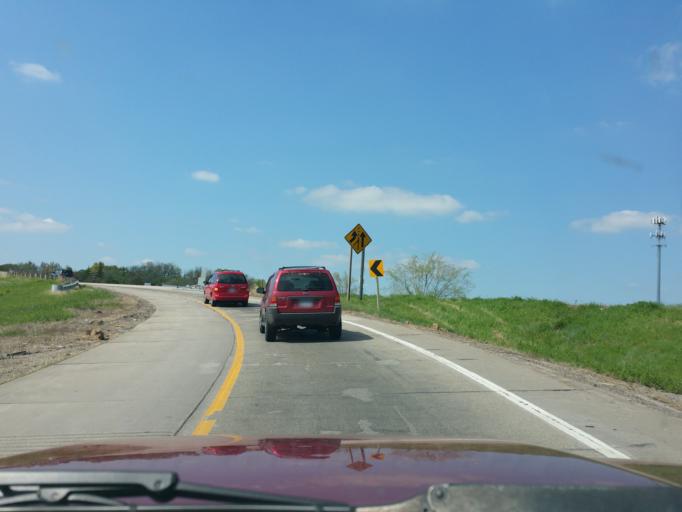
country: US
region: Kansas
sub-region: Johnson County
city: Mission
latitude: 39.0402
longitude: -94.6721
